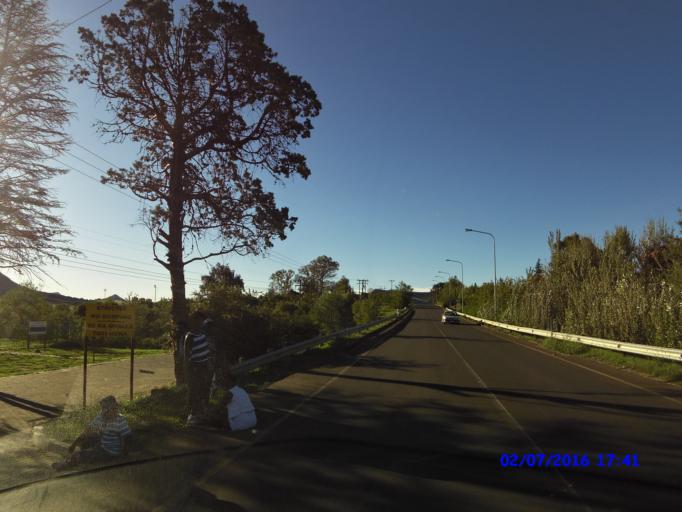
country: LS
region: Maseru
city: Maseru
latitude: -29.3129
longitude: 27.4689
